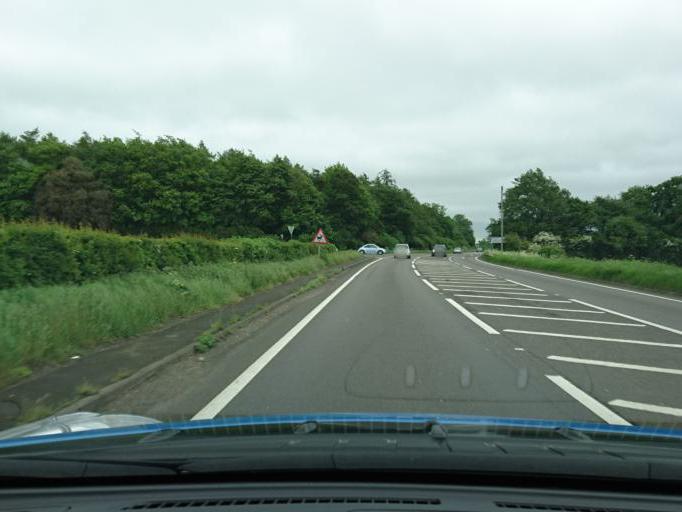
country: GB
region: England
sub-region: Oxfordshire
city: Stanford in the Vale
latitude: 51.6752
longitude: -1.5173
